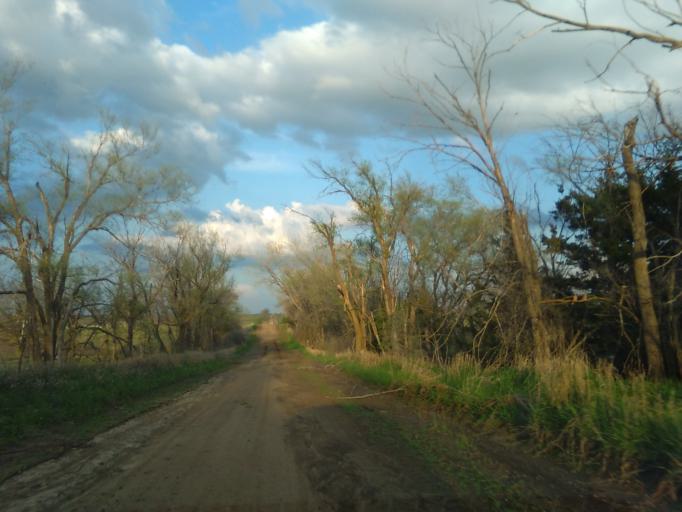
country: US
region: Nebraska
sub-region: Webster County
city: Red Cloud
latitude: 40.2054
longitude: -98.3754
